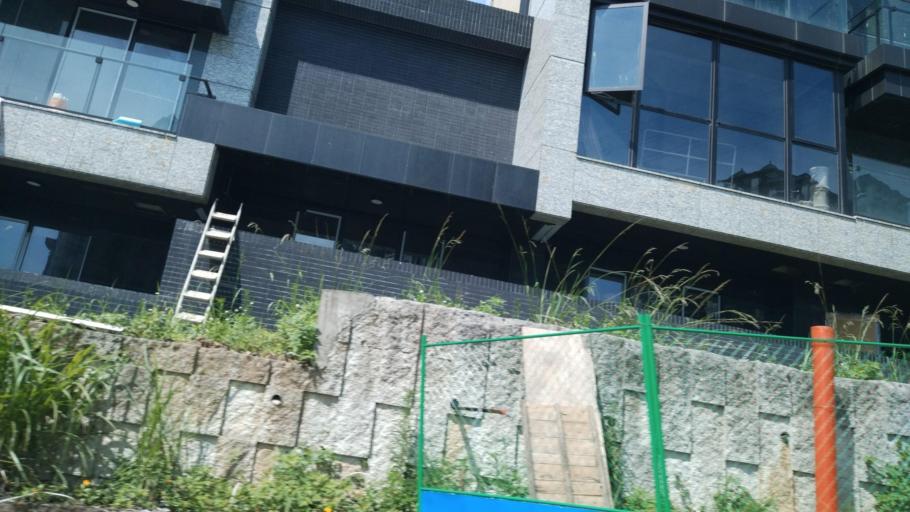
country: TW
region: Taipei
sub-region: Taipei
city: Banqiao
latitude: 24.9412
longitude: 121.5033
